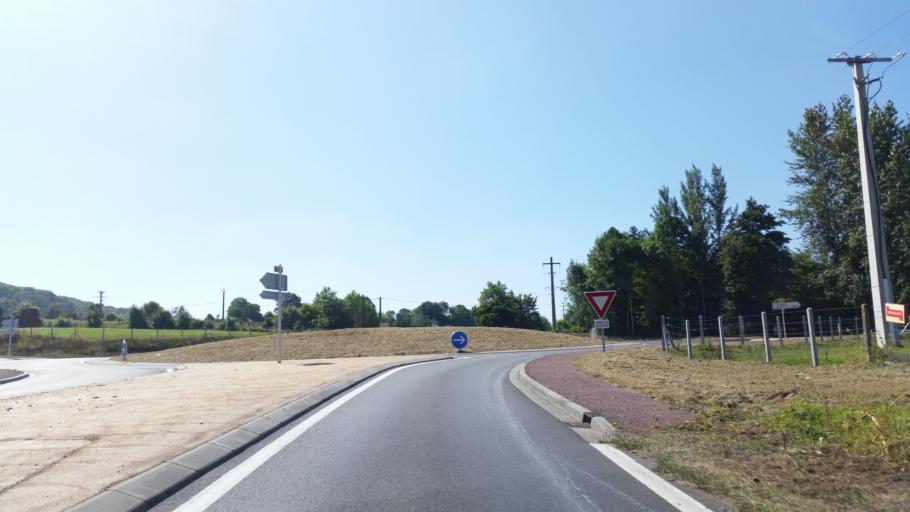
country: FR
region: Lower Normandy
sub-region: Departement du Calvados
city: Saint-Gatien-des-Bois
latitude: 49.2524
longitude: 0.2200
